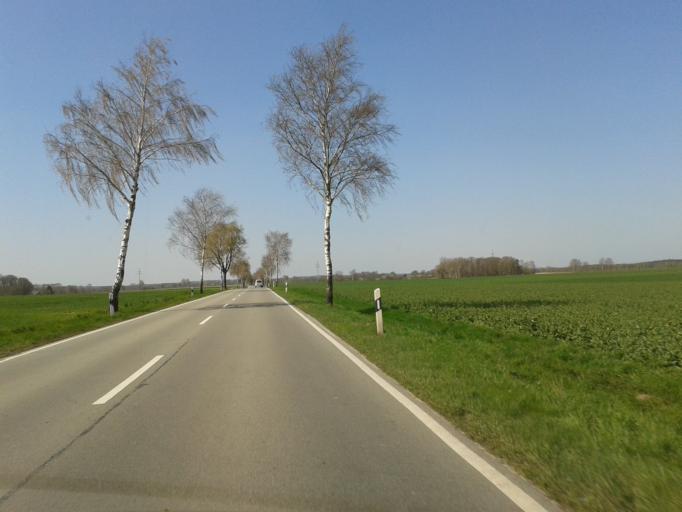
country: DE
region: Lower Saxony
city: Kusten
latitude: 52.9428
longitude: 11.0627
